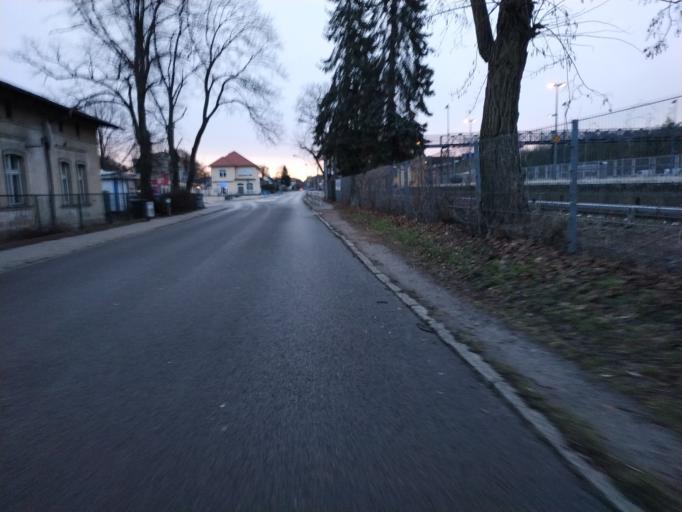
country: DE
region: Brandenburg
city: Petershagen
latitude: 52.5324
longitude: 13.8340
